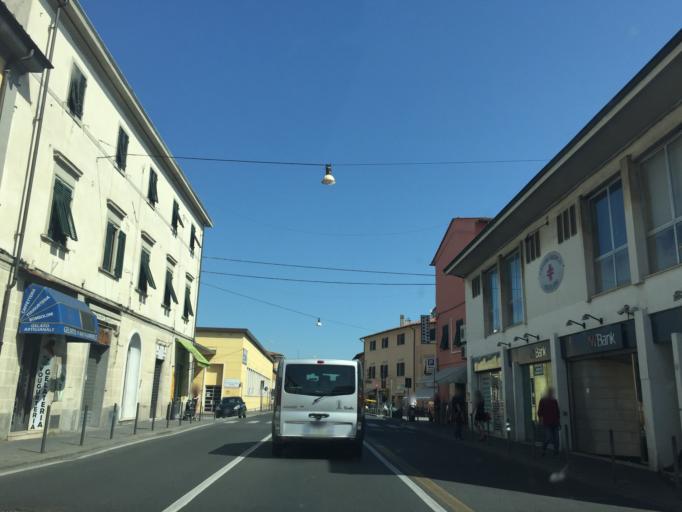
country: IT
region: Tuscany
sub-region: Province of Pisa
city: Pisa
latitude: 43.7233
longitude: 10.3921
